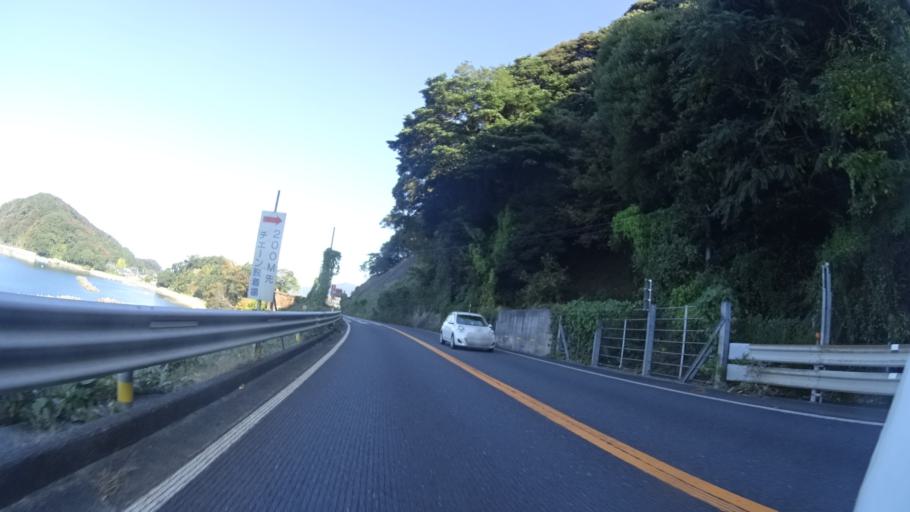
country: JP
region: Fukui
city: Tsuruga
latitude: 35.7334
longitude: 136.0979
